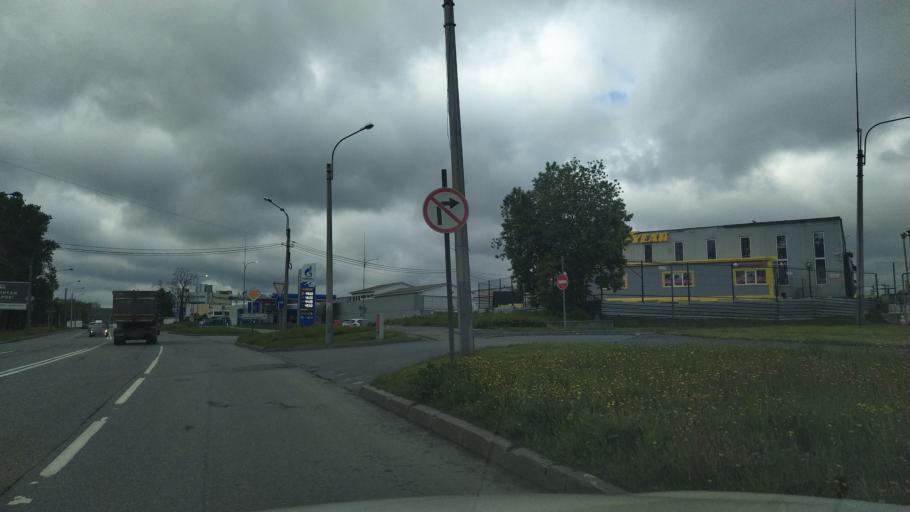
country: RU
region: St.-Petersburg
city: Krasnogvargeisky
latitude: 59.9670
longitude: 30.4715
